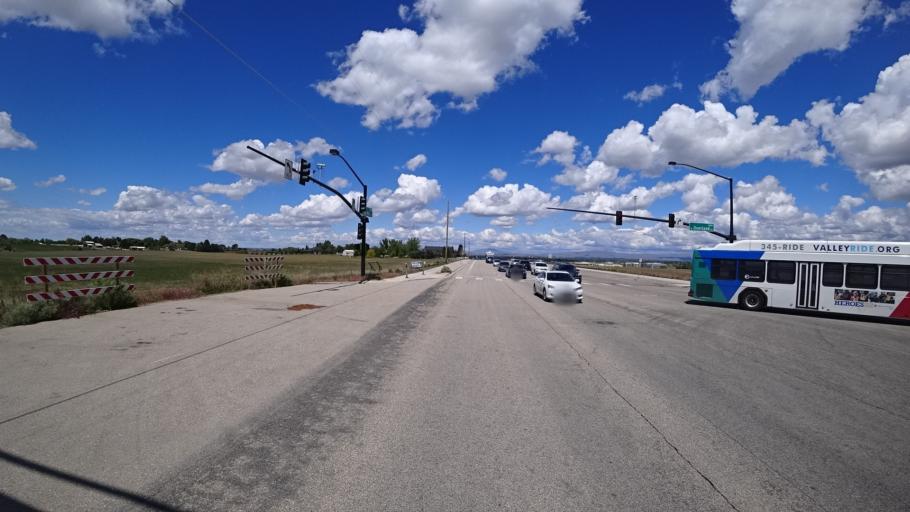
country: US
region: Idaho
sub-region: Ada County
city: Meridian
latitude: 43.5849
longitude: -116.4339
